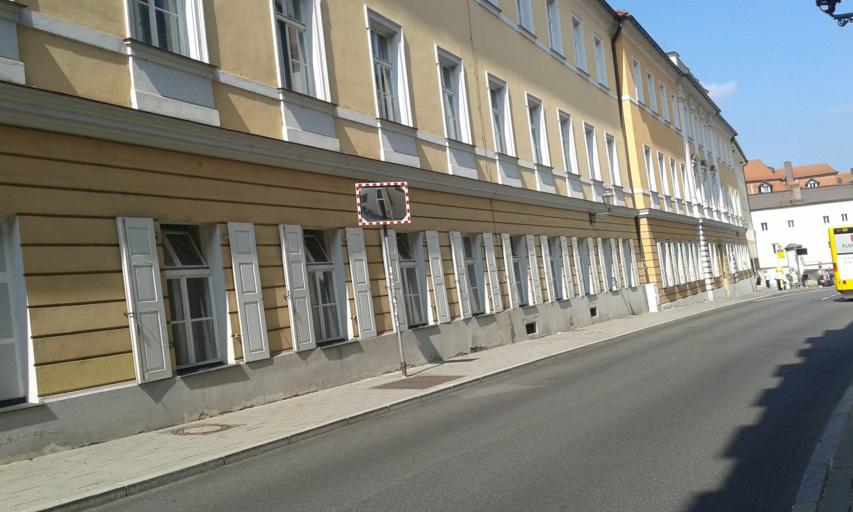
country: DE
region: Bavaria
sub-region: Upper Palatinate
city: Lappersdorf
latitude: 49.0179
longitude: 12.0890
